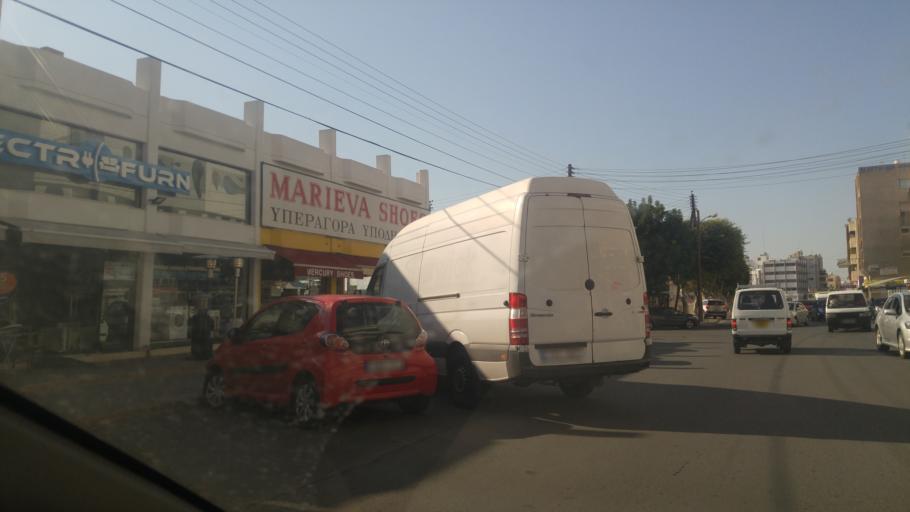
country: CY
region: Limassol
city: Limassol
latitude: 34.6922
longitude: 33.0630
